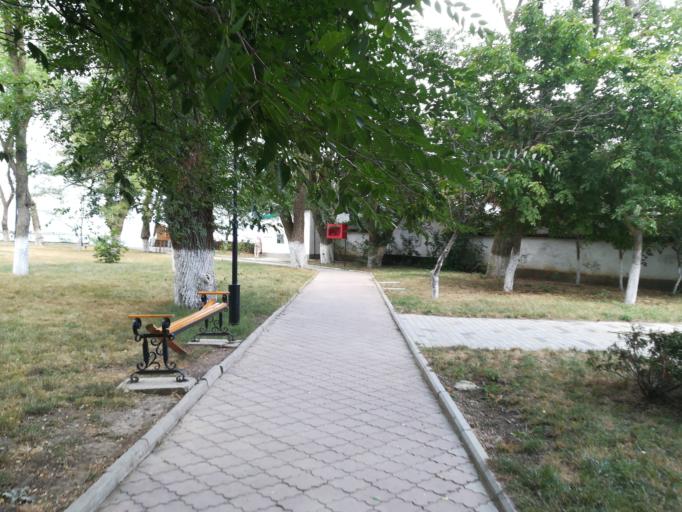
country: RU
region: Krasnodarskiy
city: Taman'
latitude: 45.2176
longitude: 36.7250
